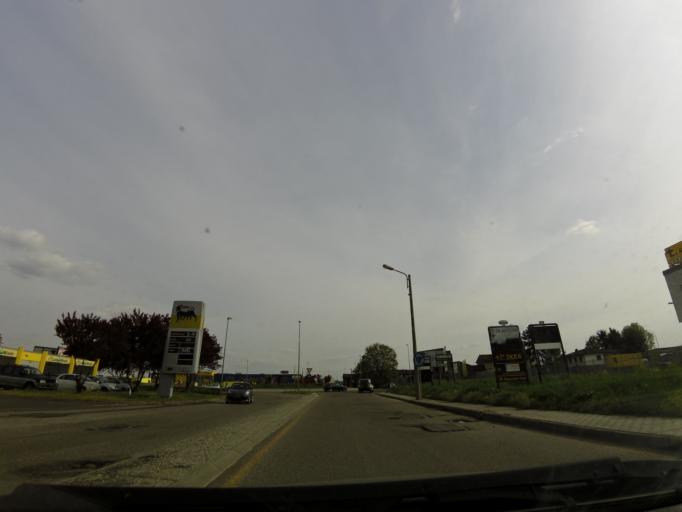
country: IT
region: Lombardy
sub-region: Citta metropolitana di Milano
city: Civesio
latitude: 45.3923
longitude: 9.2572
